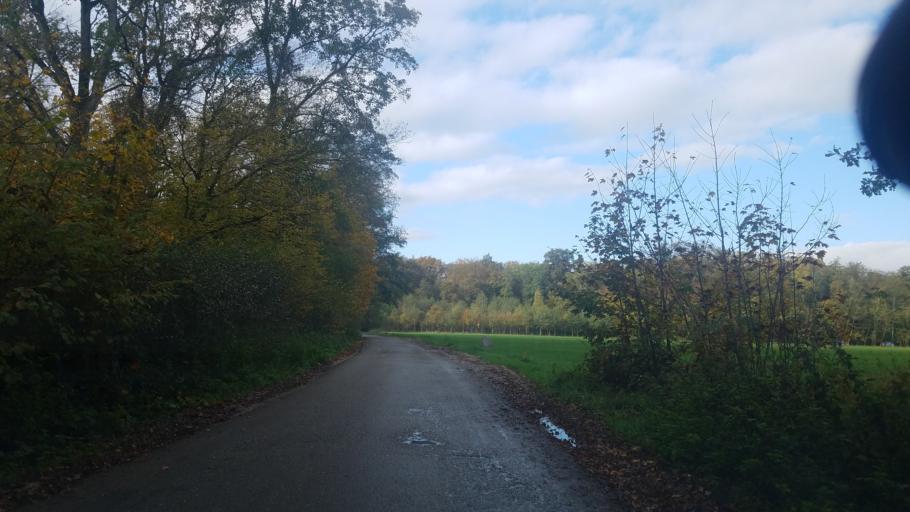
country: DE
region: Baden-Wuerttemberg
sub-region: Karlsruhe Region
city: Lichtenau
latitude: 48.6593
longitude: 8.0050
